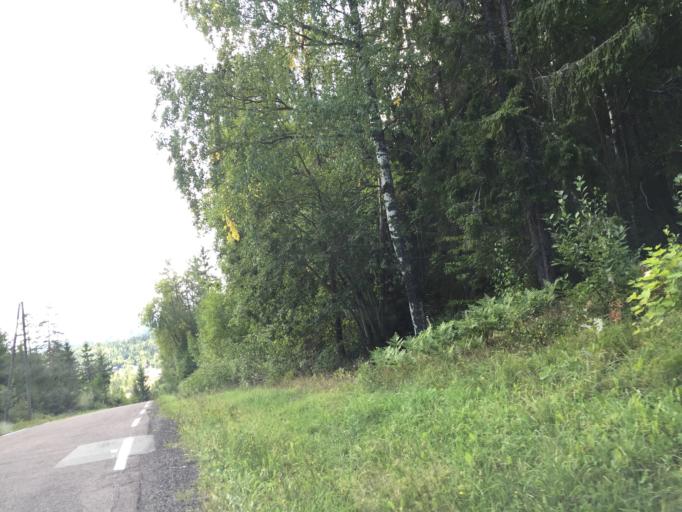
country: NO
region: Vestfold
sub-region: Hof
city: Hof
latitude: 59.4323
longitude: 10.1417
